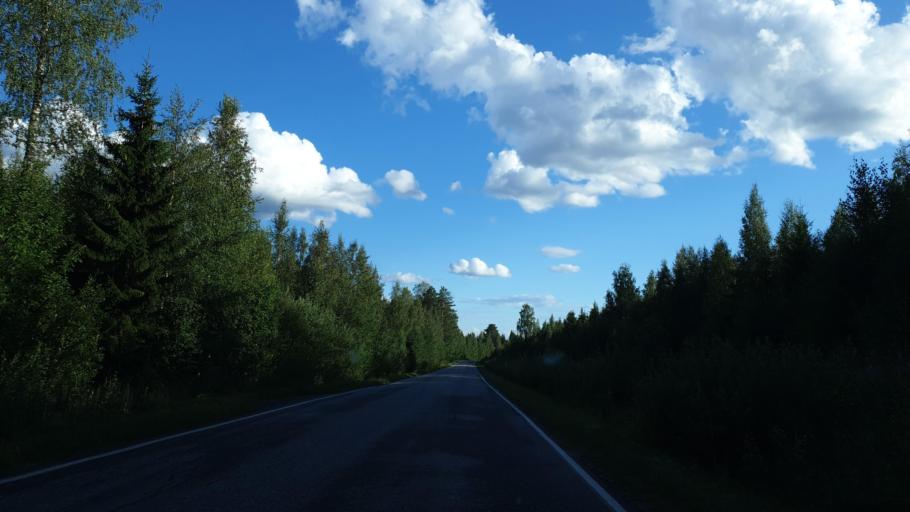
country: FI
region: Northern Savo
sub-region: Koillis-Savo
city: Kaavi
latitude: 62.9918
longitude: 28.5043
